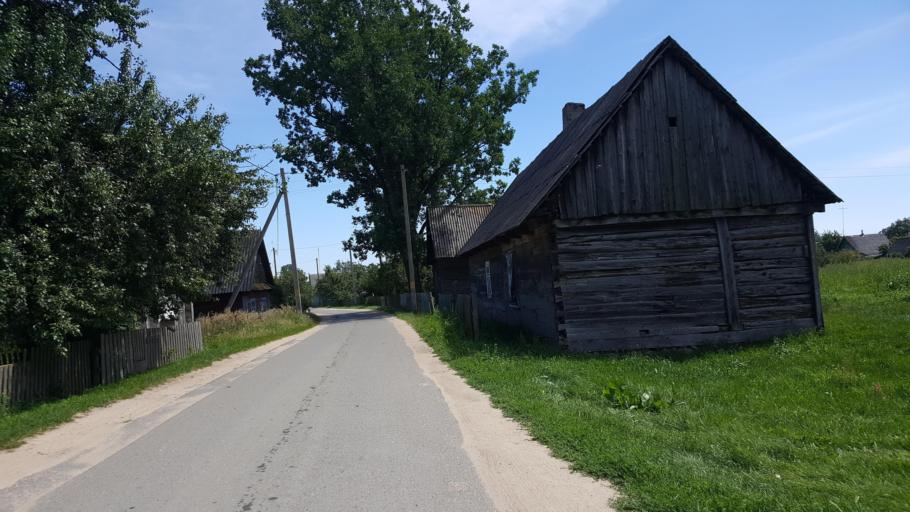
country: BY
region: Brest
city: Pruzhany
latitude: 52.5561
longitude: 24.2089
